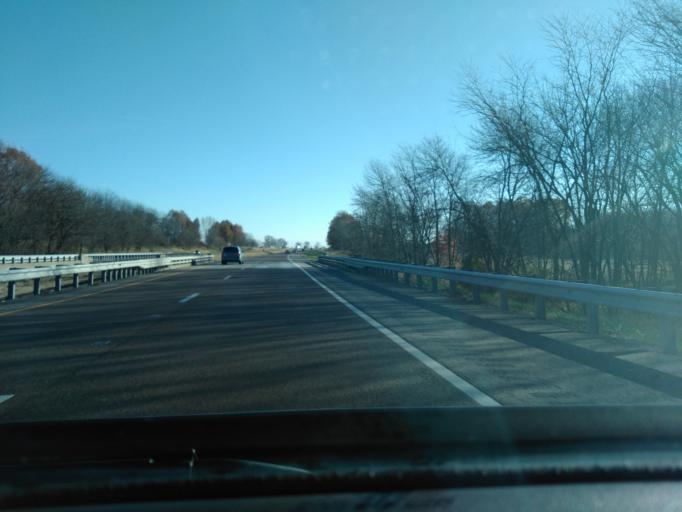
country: US
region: Illinois
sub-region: Madison County
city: Troy
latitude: 38.7620
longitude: -89.8246
